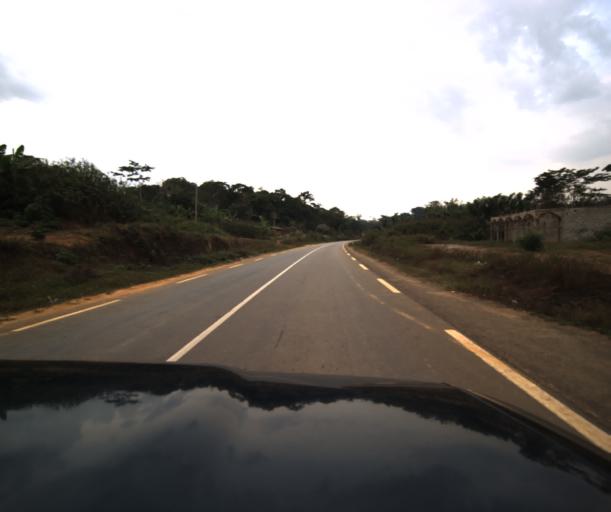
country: CM
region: Centre
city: Mbankomo
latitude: 3.7643
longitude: 11.4057
